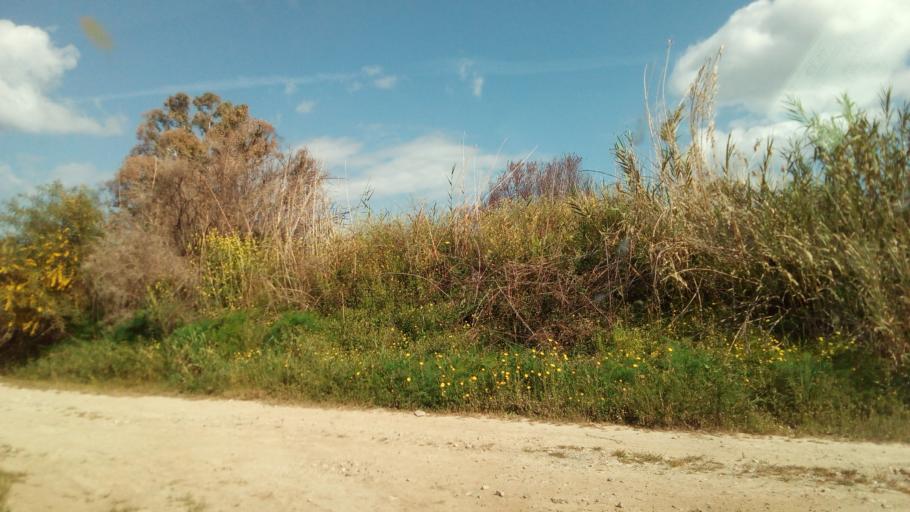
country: CY
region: Pafos
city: Polis
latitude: 35.0299
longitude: 32.4252
